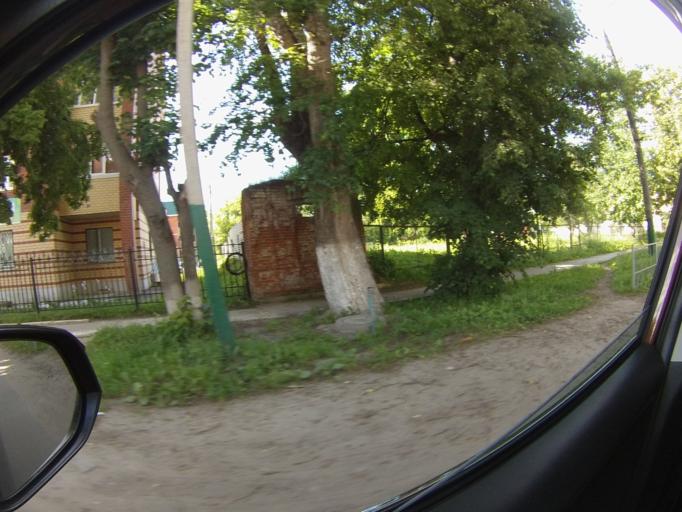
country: RU
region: Orjol
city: Mtsensk
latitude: 53.2784
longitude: 36.5707
